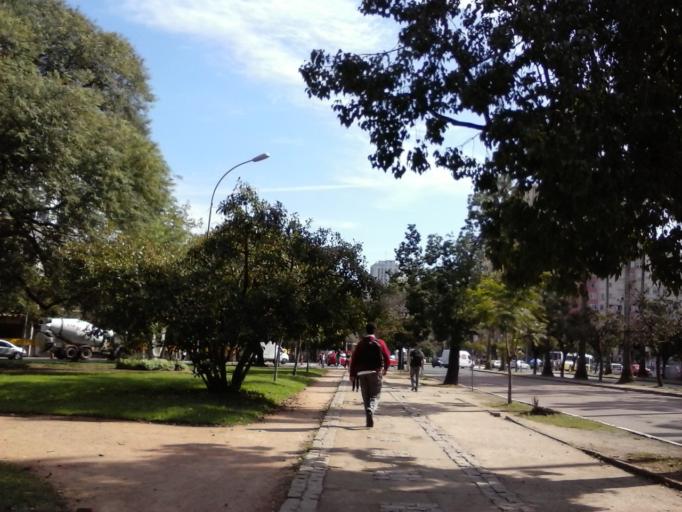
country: BR
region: Rio Grande do Sul
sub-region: Porto Alegre
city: Porto Alegre
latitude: -30.0330
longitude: -51.2183
